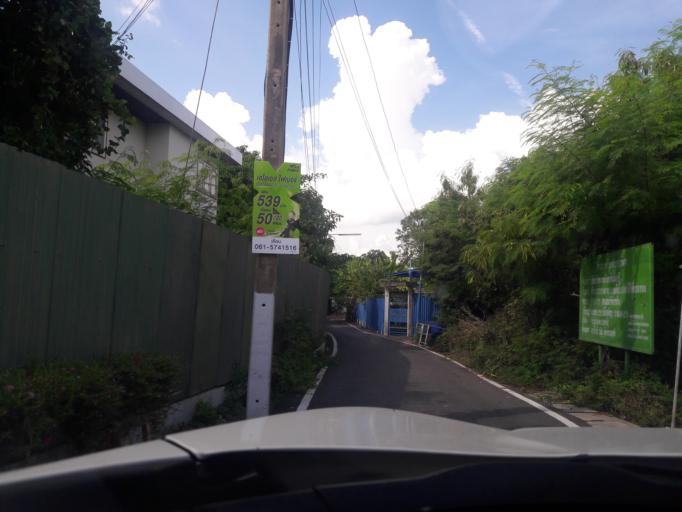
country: TH
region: Lop Buri
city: Ban Mi
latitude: 15.0477
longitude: 100.5374
